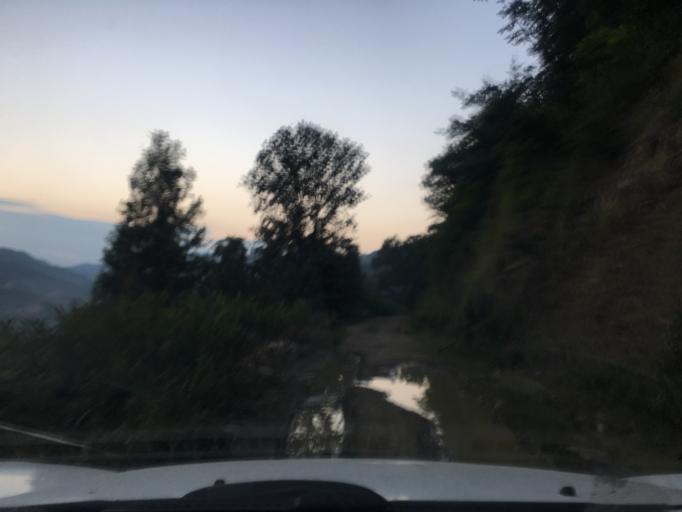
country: CN
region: Guangxi Zhuangzu Zizhiqu
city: Xinzhou
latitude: 25.3556
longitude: 105.7426
